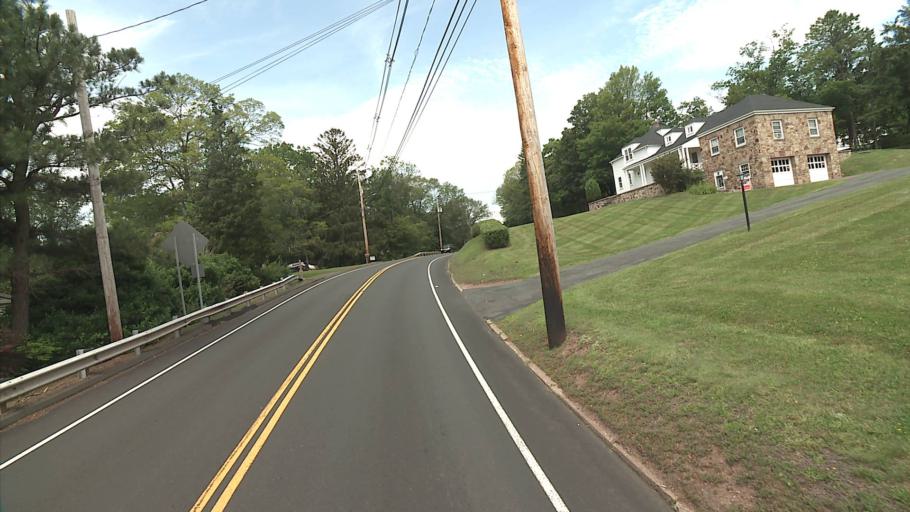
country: US
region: Connecticut
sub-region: New Haven County
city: Wallingford Center
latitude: 41.3940
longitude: -72.7936
